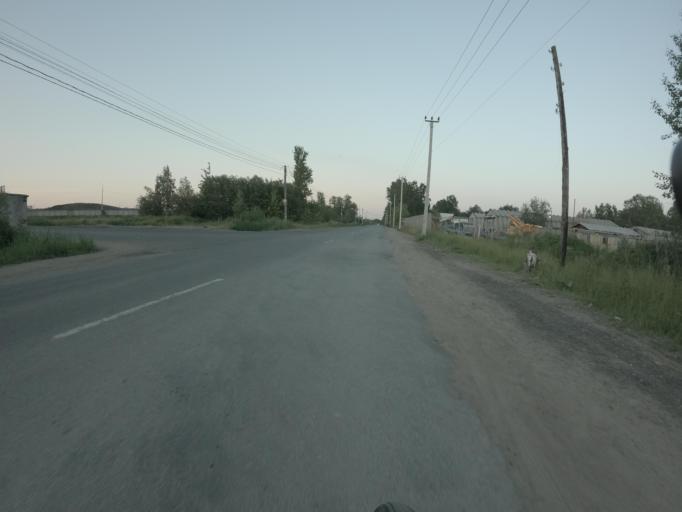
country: RU
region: St.-Petersburg
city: Dachnoye
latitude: 59.8229
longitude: 30.2844
